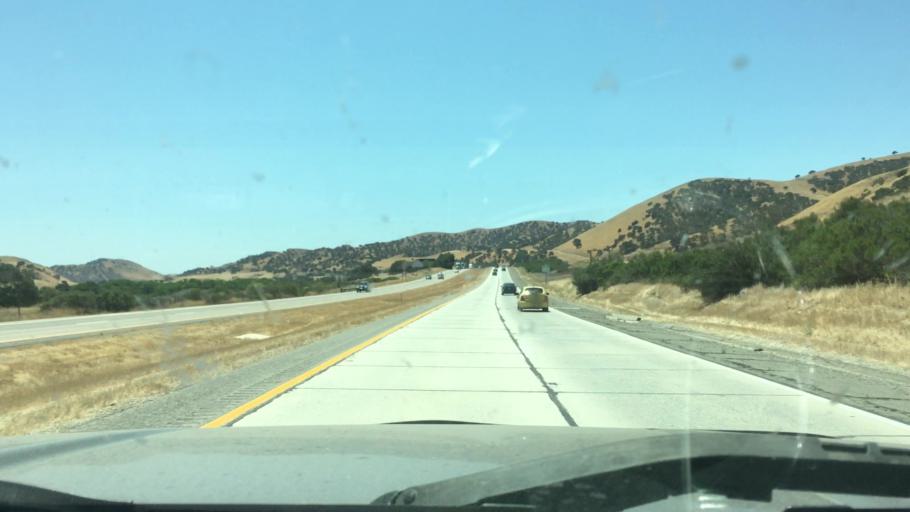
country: US
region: California
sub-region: San Luis Obispo County
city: Lake Nacimiento
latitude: 35.9397
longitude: -120.8734
